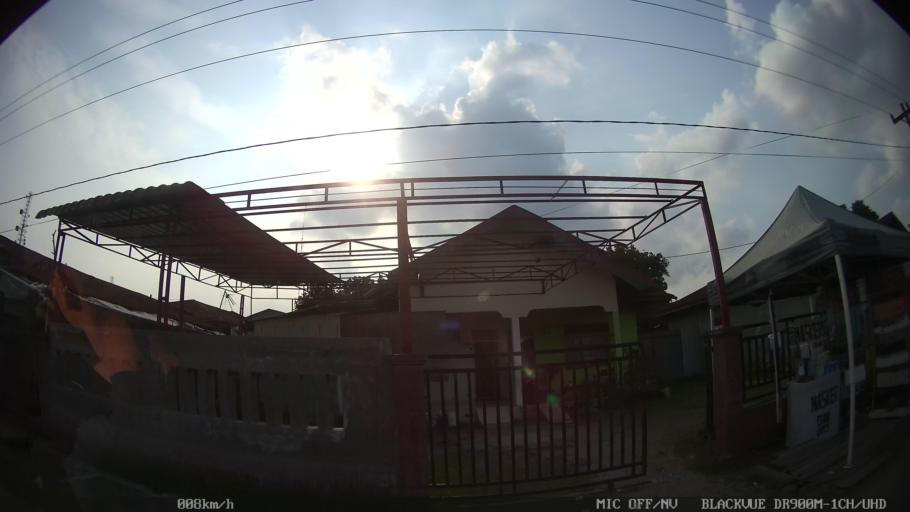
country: ID
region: North Sumatra
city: Medan
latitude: 3.5884
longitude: 98.7410
